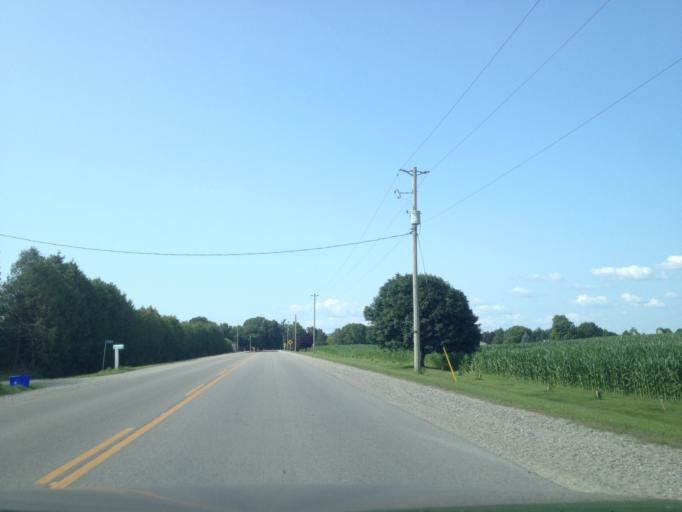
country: CA
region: Ontario
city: Aylmer
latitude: 42.7248
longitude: -80.8586
